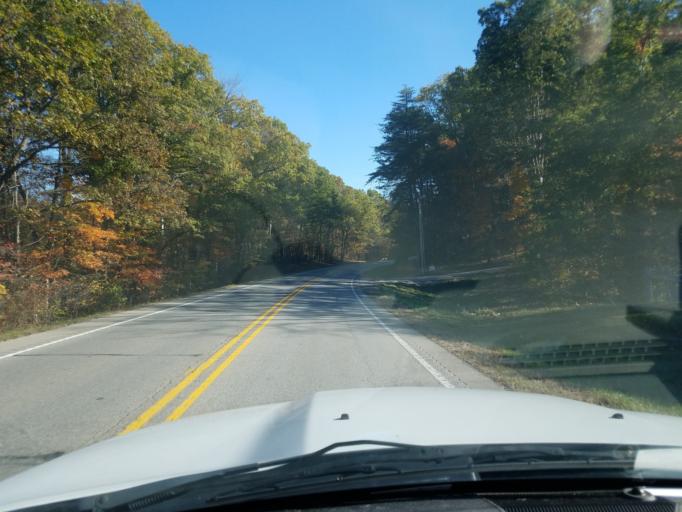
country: US
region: Indiana
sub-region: Jennings County
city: Country Squire Lakes
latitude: 38.9782
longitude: -85.7177
